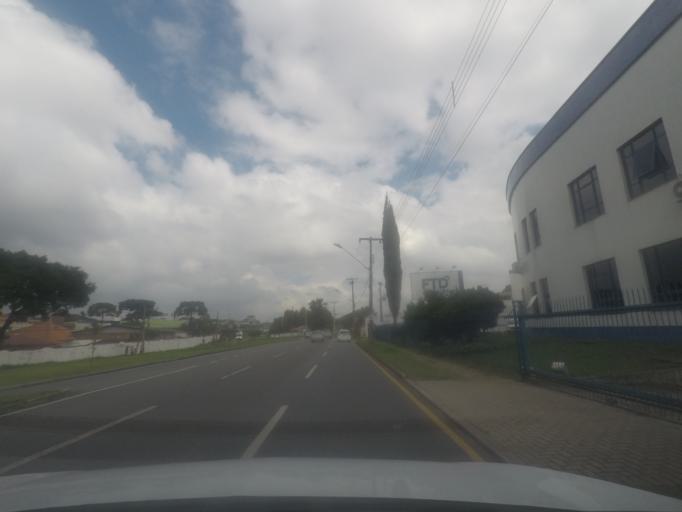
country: BR
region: Parana
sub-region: Curitiba
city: Curitiba
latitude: -25.4520
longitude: -49.2580
